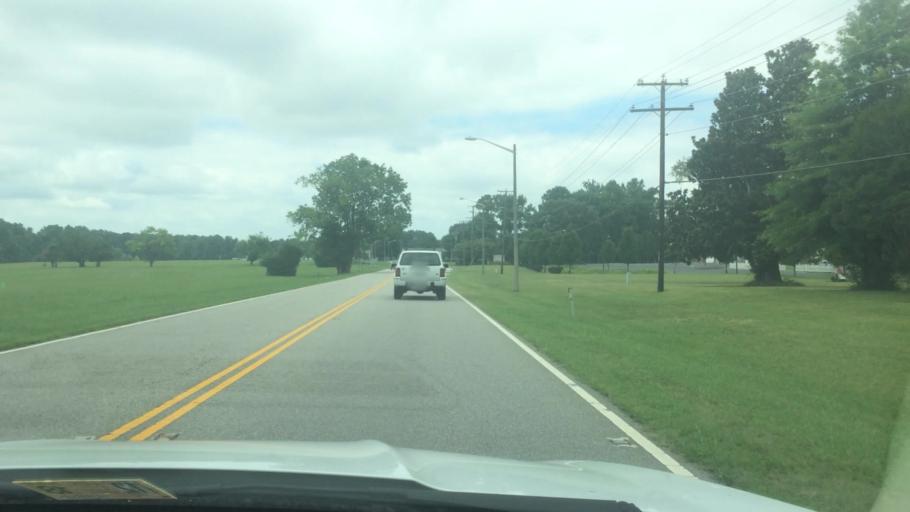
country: US
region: Virginia
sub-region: York County
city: Yorktown
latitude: 37.2143
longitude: -76.5701
